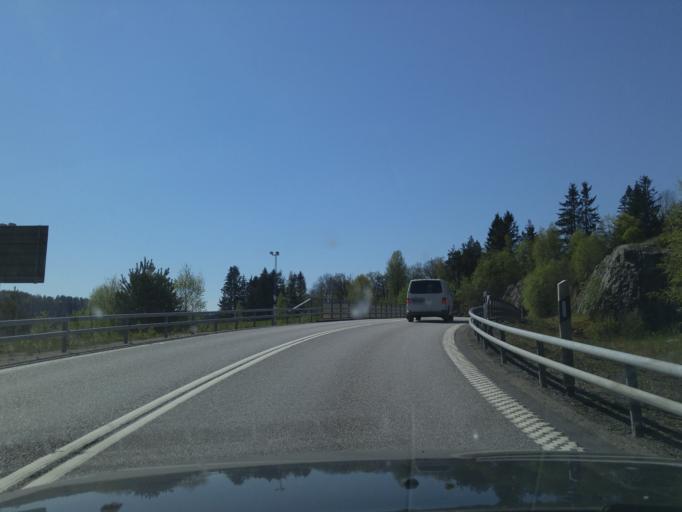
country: SE
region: Vaestra Goetaland
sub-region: Munkedals Kommun
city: Munkedal
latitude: 58.4882
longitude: 11.5874
